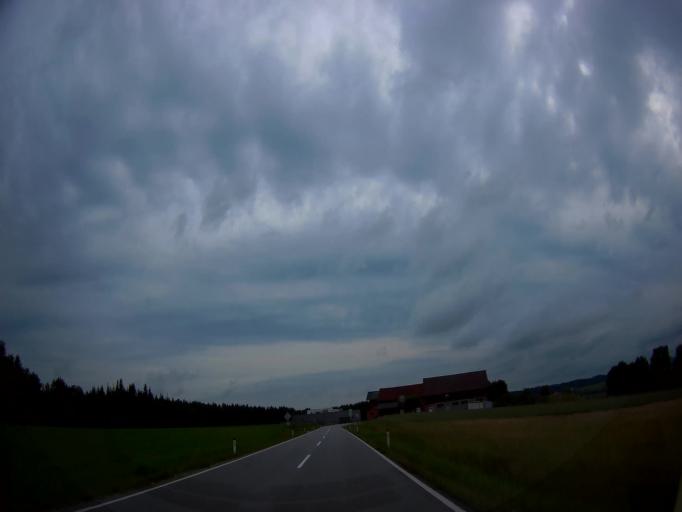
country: AT
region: Upper Austria
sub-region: Politischer Bezirk Braunau am Inn
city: Altheim
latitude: 48.1950
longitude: 13.1471
